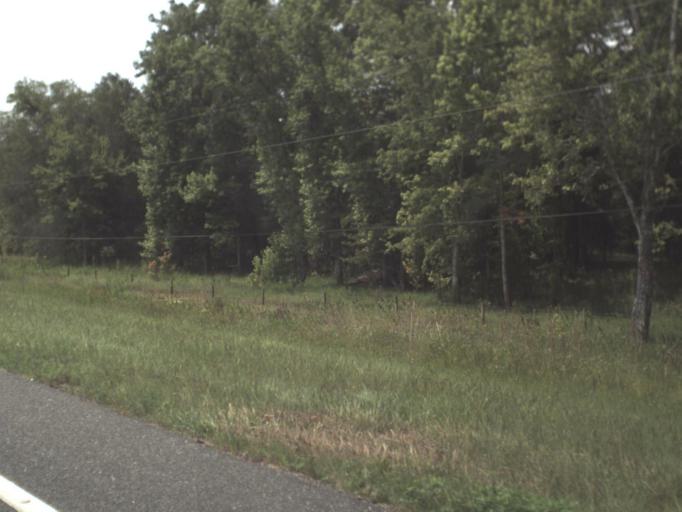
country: US
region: Florida
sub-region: Levy County
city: Chiefland
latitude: 29.4352
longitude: -82.8346
